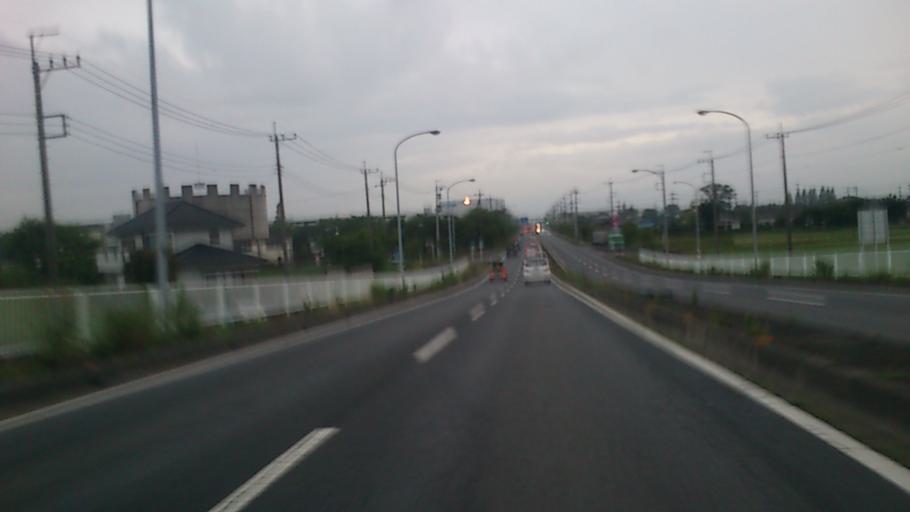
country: JP
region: Saitama
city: Hanyu
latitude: 36.1599
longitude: 139.5394
